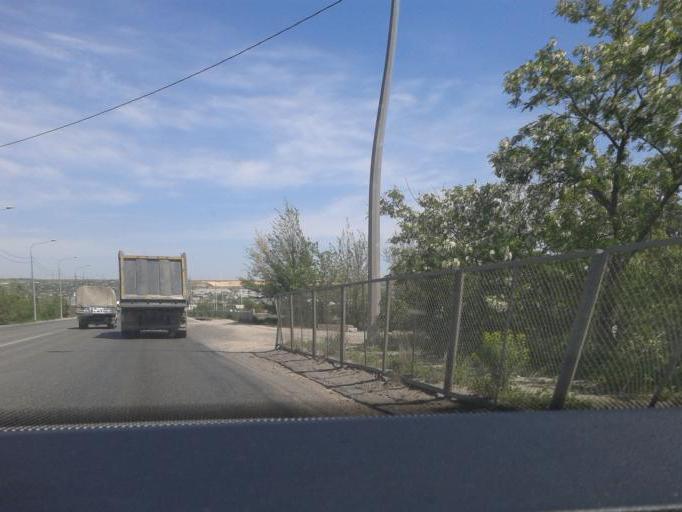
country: RU
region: Volgograd
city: Gorodishche
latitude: 48.7863
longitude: 44.5204
